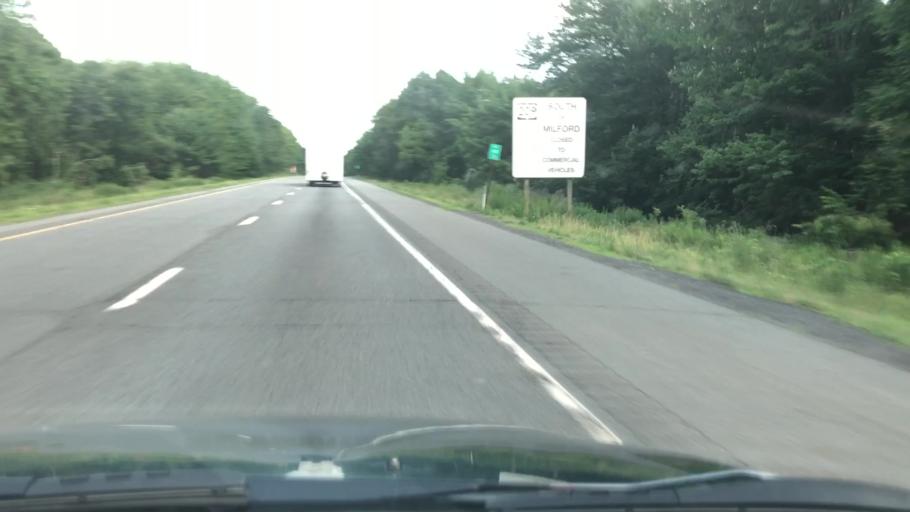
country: US
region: Pennsylvania
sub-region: Pike County
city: Milford
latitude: 41.3366
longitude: -74.8646
